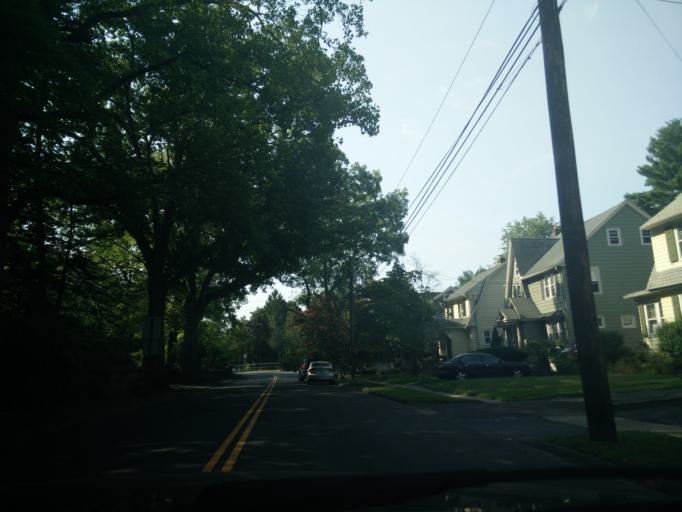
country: US
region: Connecticut
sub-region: Fairfield County
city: Bridgeport
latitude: 41.1990
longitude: -73.2307
